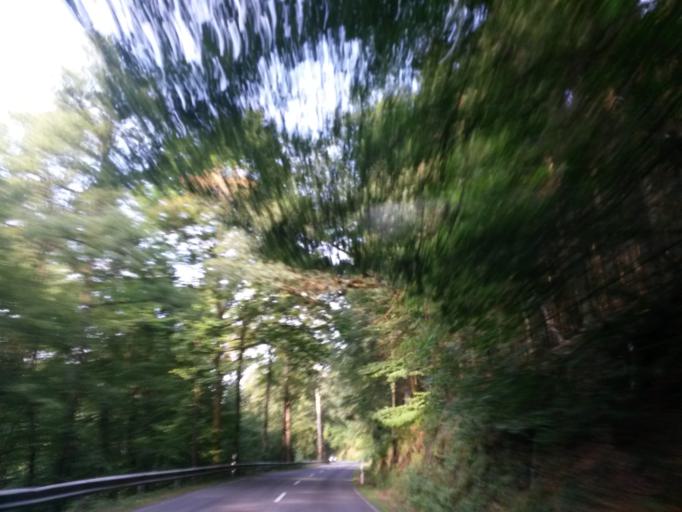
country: DE
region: North Rhine-Westphalia
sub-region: Regierungsbezirk Koln
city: Lindlar
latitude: 51.0446
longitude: 7.4527
